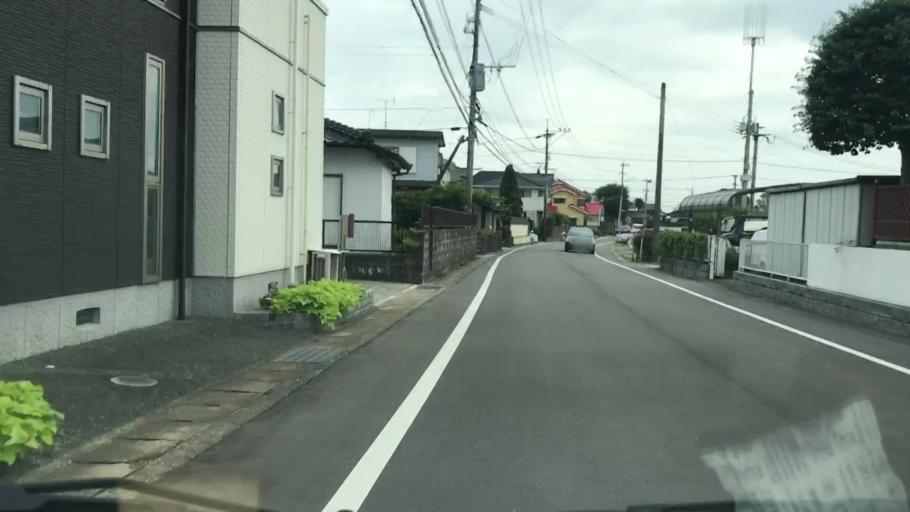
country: JP
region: Saga Prefecture
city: Saga-shi
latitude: 33.2742
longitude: 130.2636
